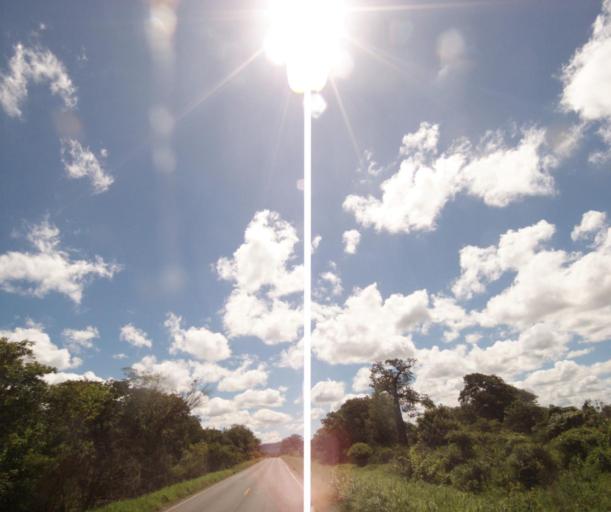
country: BR
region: Bahia
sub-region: Sao Felix Do Coribe
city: Santa Maria da Vitoria
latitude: -13.4072
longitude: -44.1647
